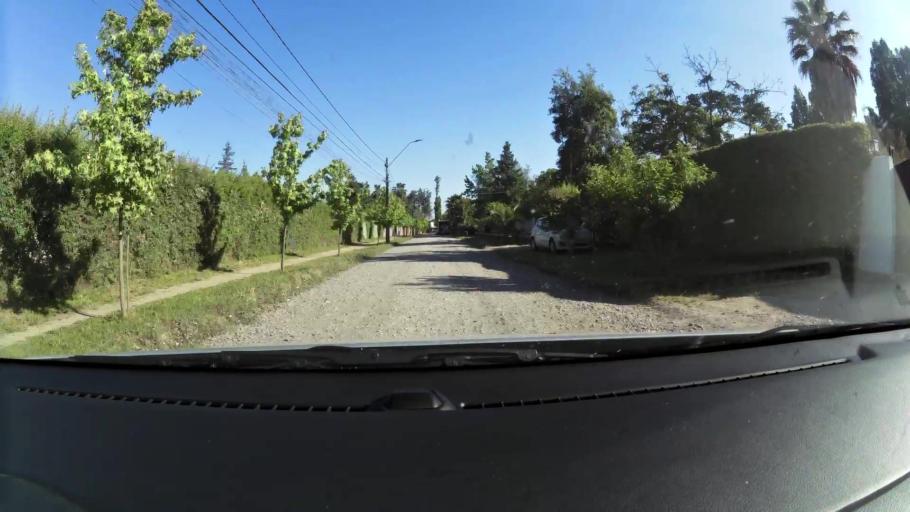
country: CL
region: Santiago Metropolitan
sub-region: Provincia de Maipo
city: San Bernardo
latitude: -33.6411
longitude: -70.6855
